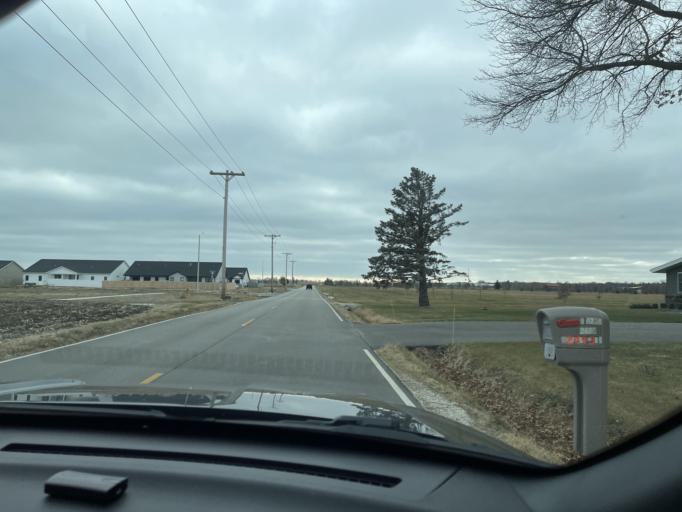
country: US
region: Illinois
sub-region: Sangamon County
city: Jerome
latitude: 39.7640
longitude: -89.7533
